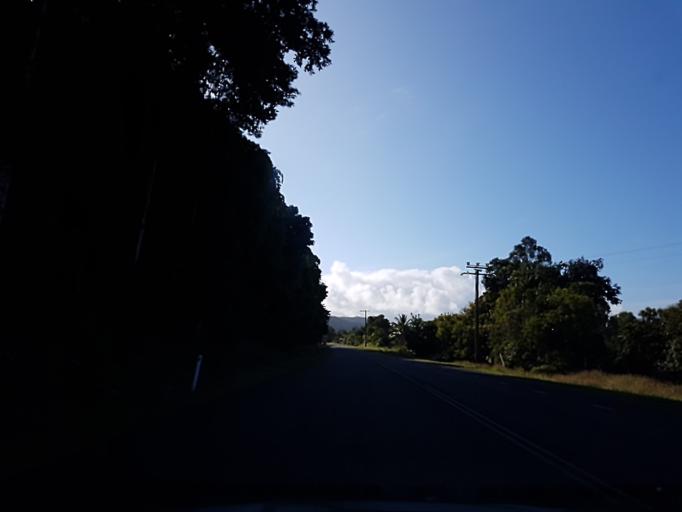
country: AU
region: Queensland
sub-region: Cairns
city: Port Douglas
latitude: -16.3630
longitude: 145.4120
